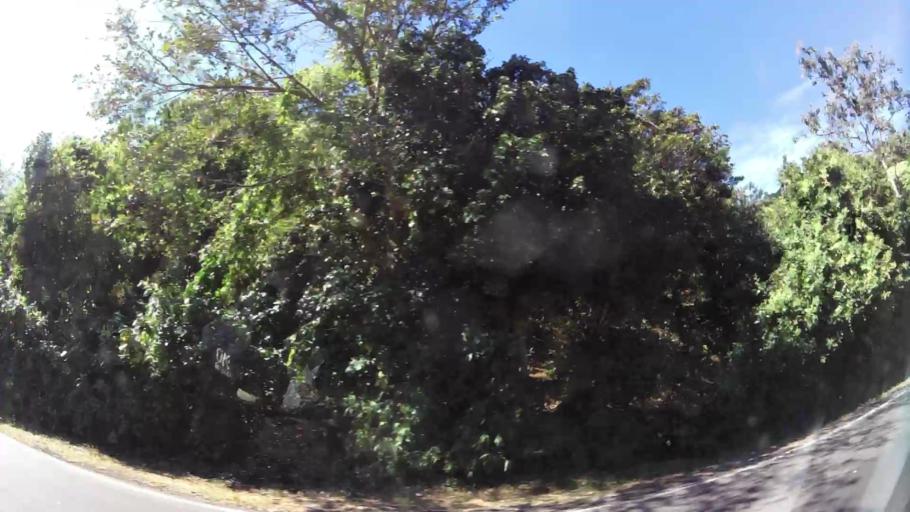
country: SV
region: Sonsonate
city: Juayua
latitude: 13.8417
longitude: -89.7645
